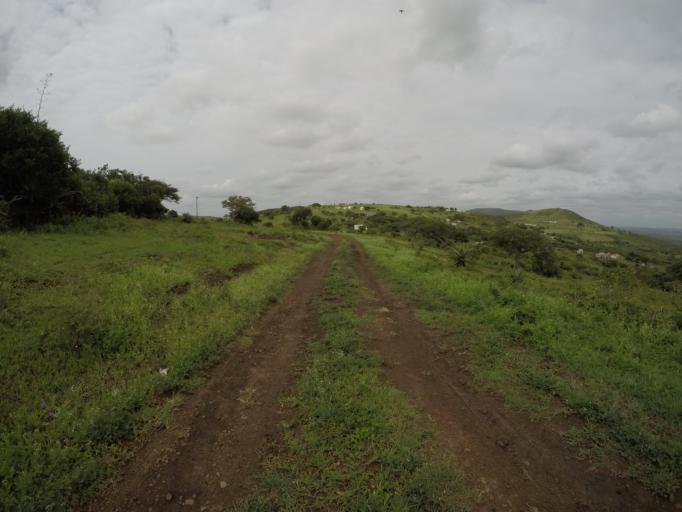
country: ZA
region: KwaZulu-Natal
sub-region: uThungulu District Municipality
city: Empangeni
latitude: -28.6120
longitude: 31.8994
